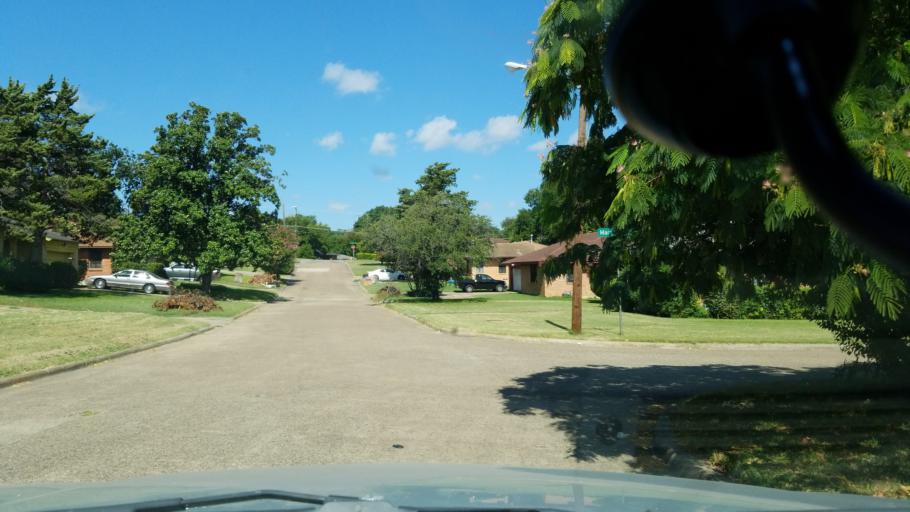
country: US
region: Texas
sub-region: Dallas County
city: Cockrell Hill
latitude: 32.6814
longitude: -96.8131
